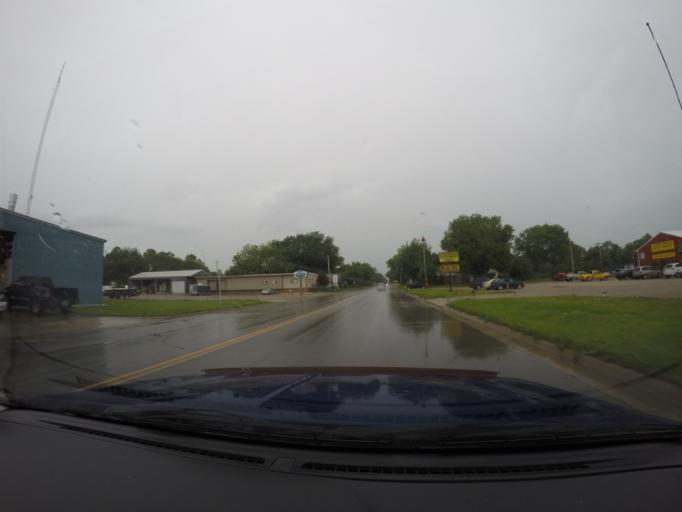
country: US
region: Kansas
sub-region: Cloud County
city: Concordia
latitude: 39.5716
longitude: -97.6454
